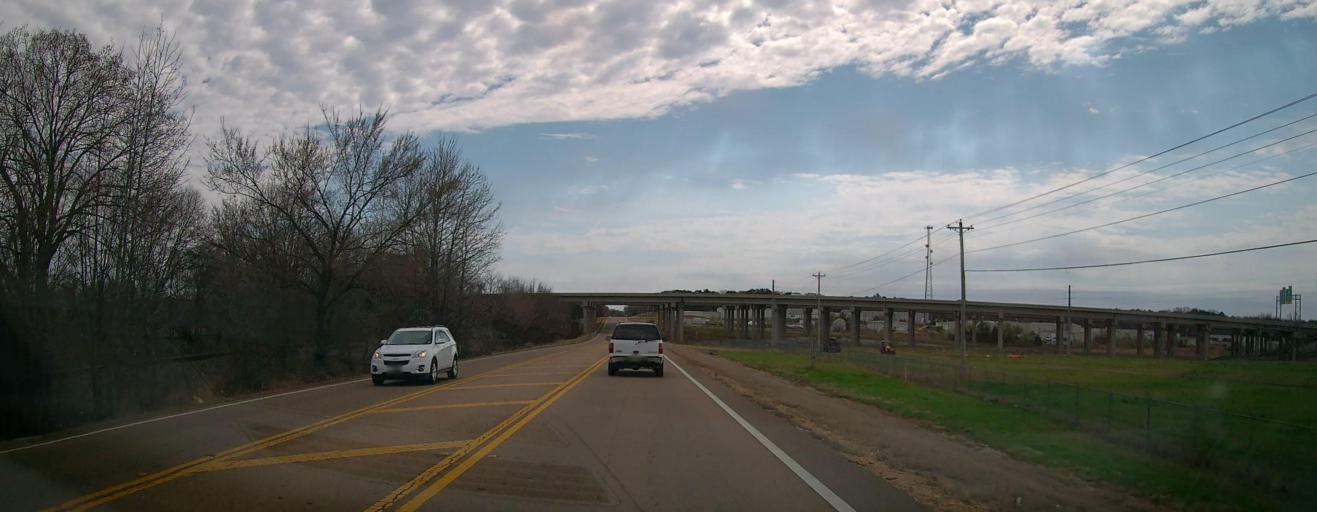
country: US
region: Mississippi
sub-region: Marshall County
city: Byhalia
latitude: 34.8848
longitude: -89.7207
